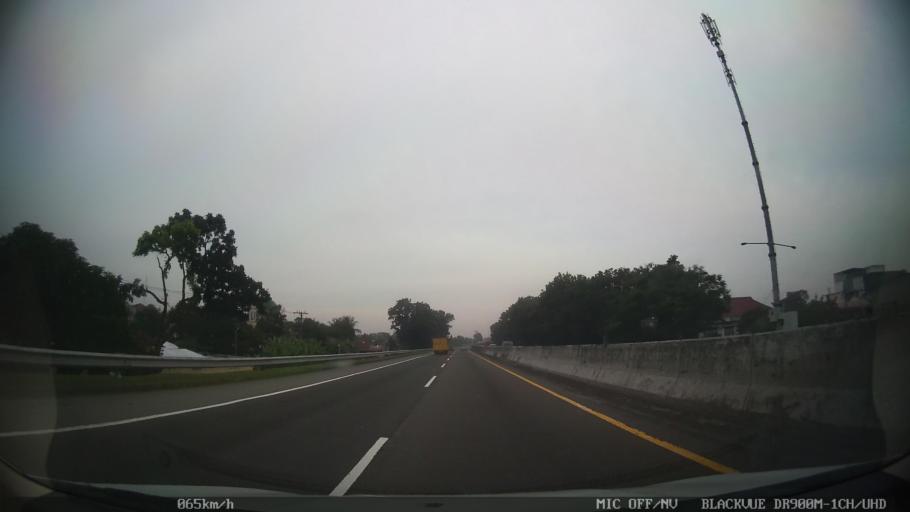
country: ID
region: North Sumatra
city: Medan
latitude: 3.5723
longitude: 98.7255
